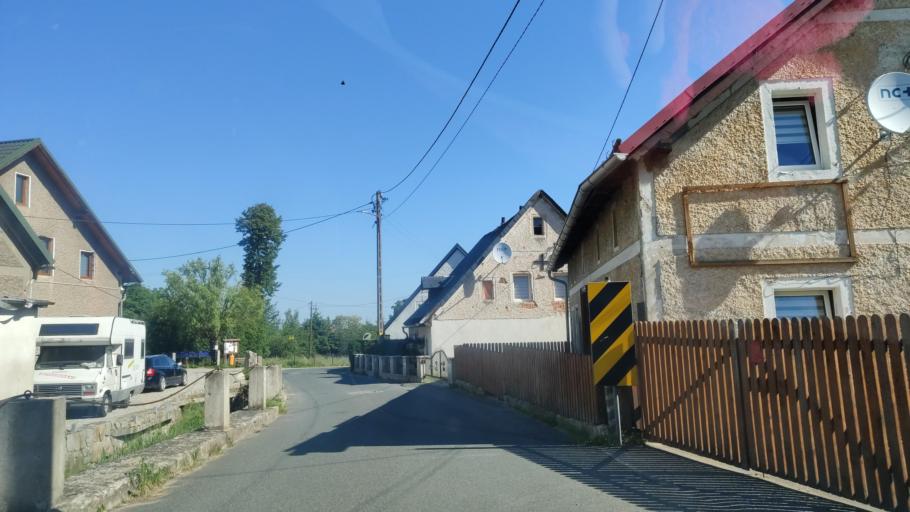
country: PL
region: Lower Silesian Voivodeship
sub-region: Powiat jeleniogorski
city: Karpacz
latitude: 50.7877
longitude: 15.7783
